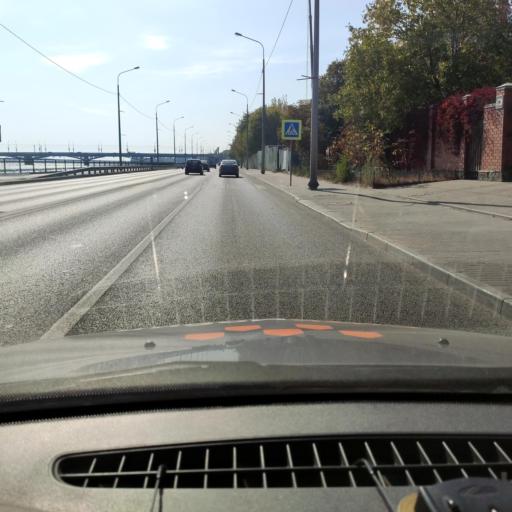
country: RU
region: Voronezj
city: Voronezh
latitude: 51.6728
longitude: 39.2244
